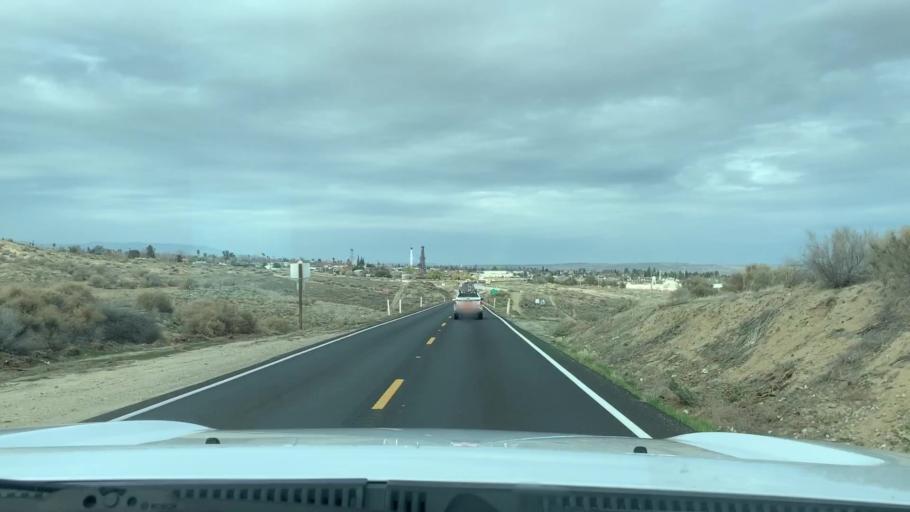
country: US
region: California
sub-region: Kern County
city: South Taft
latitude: 35.1278
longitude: -119.4419
